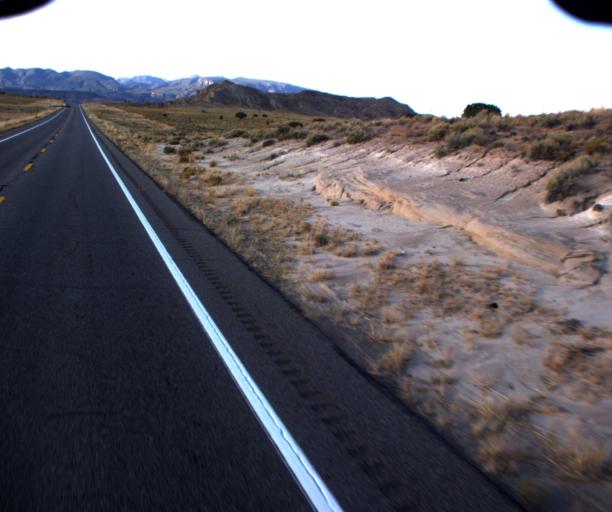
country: US
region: New Mexico
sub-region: San Juan County
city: Shiprock
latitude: 36.9542
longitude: -109.0694
